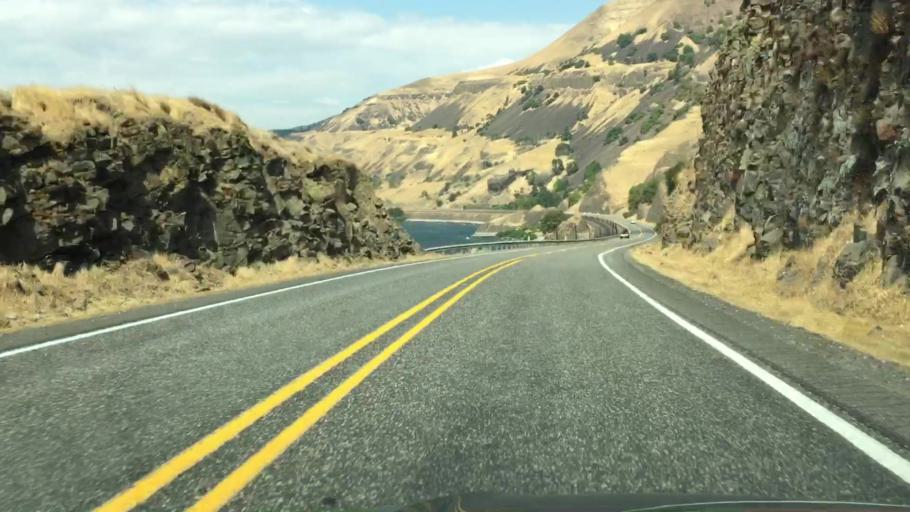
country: US
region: Oregon
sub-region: Wasco County
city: Chenoweth
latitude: 45.6685
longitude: -121.2070
